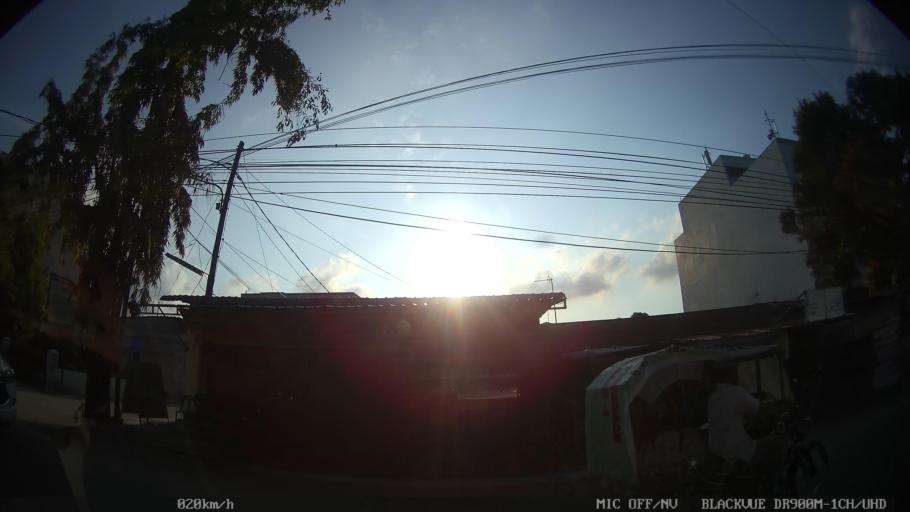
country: ID
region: North Sumatra
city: Medan
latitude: 3.6234
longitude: 98.6650
